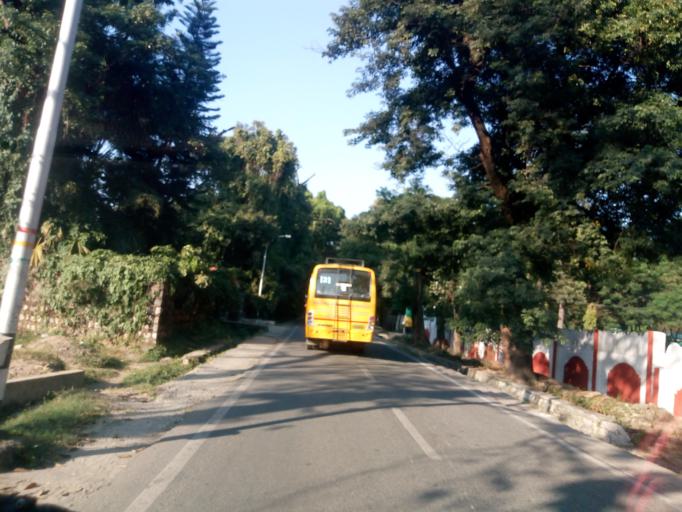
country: IN
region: Uttarakhand
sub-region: Dehradun
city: Dehradun
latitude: 30.3520
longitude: 78.0346
